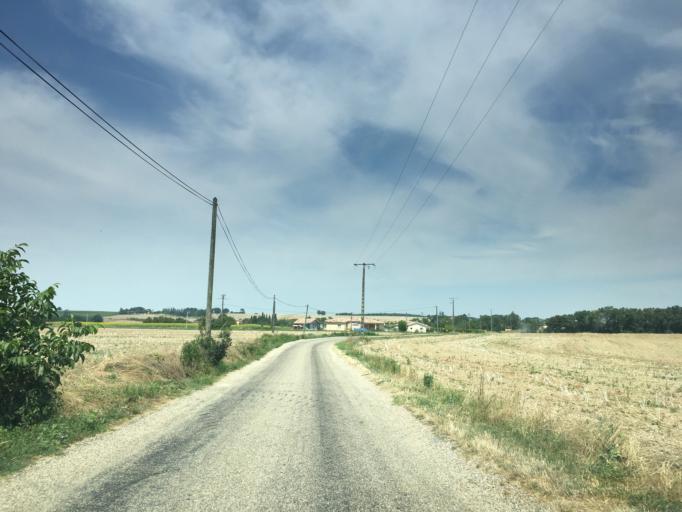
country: FR
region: Midi-Pyrenees
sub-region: Departement du Gers
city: Jegun
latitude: 43.8044
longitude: 0.4996
